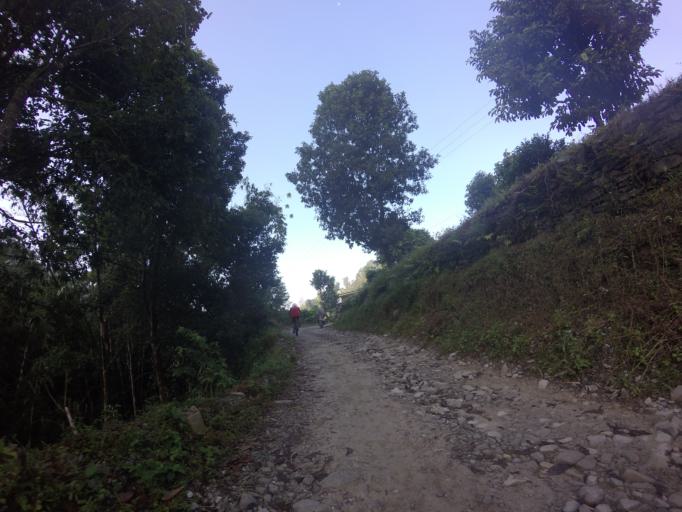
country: NP
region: Western Region
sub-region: Gandaki Zone
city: Pokhara
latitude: 28.2531
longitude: 84.0093
